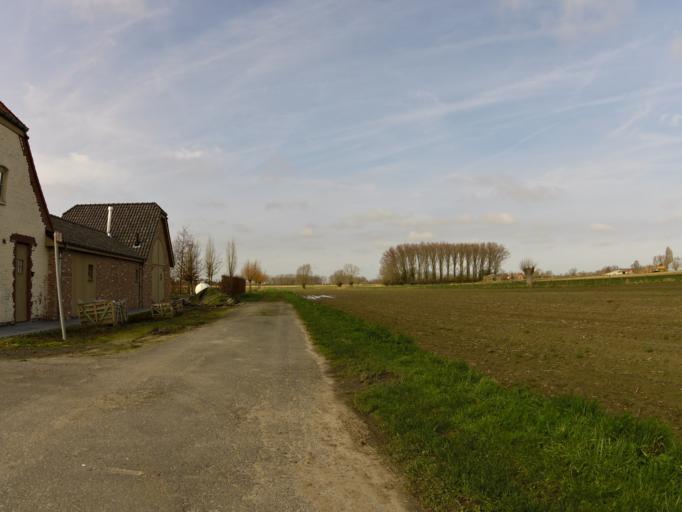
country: BE
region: Flanders
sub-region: Provincie West-Vlaanderen
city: Diksmuide
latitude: 50.9733
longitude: 2.8680
